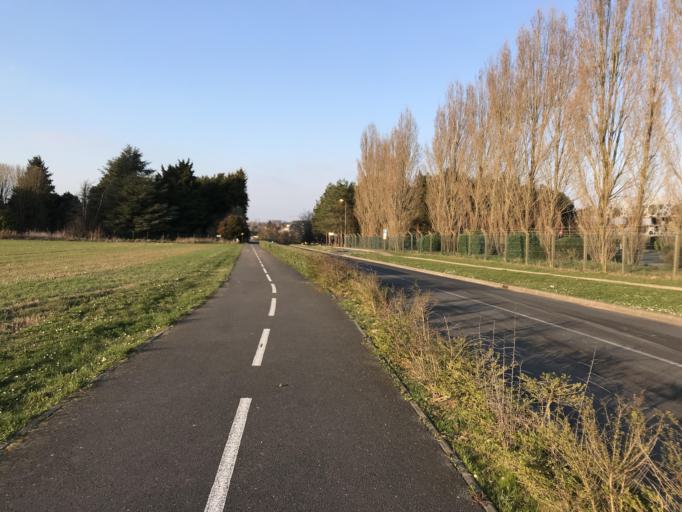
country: FR
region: Ile-de-France
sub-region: Departement de l'Essonne
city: Nozay
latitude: 48.6698
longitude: 2.2368
